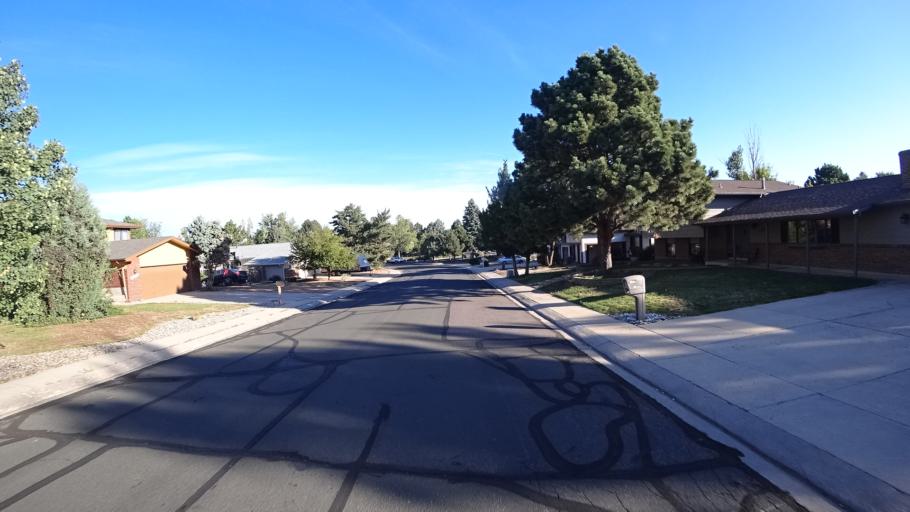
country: US
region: Colorado
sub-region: El Paso County
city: Cimarron Hills
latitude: 38.8852
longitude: -104.7654
